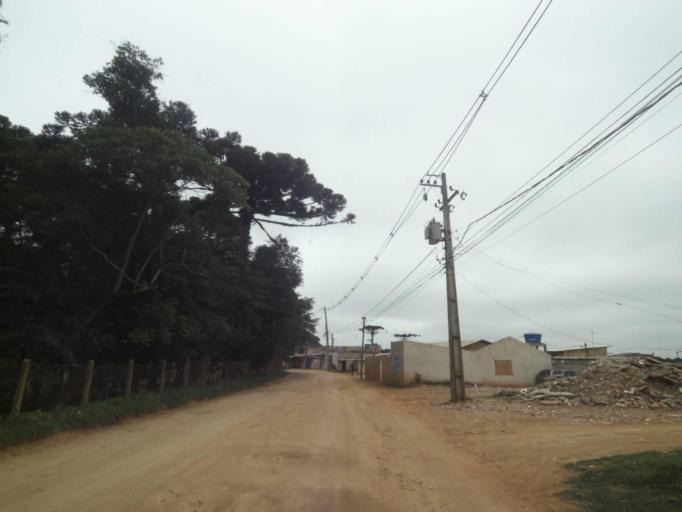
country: BR
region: Parana
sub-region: Araucaria
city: Araucaria
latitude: -25.5105
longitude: -49.3530
